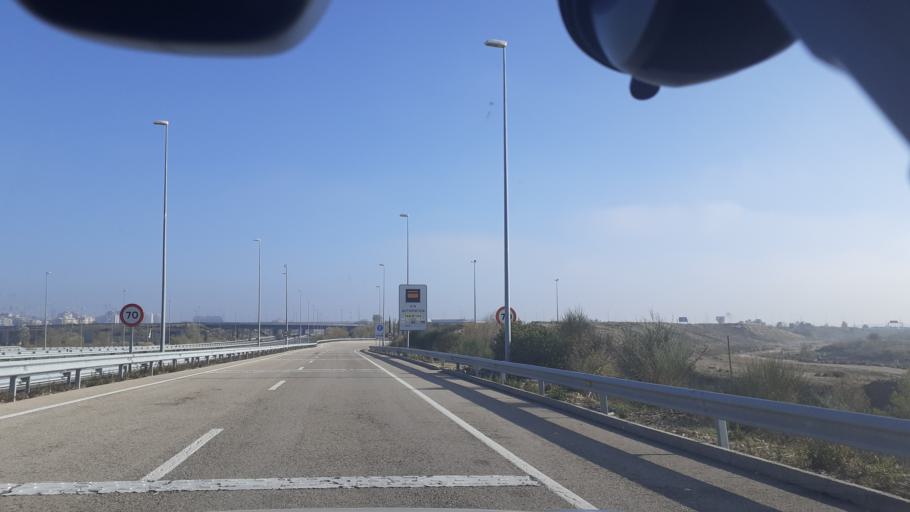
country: ES
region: Madrid
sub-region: Provincia de Madrid
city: Vicalvaro
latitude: 40.4044
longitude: -3.5798
